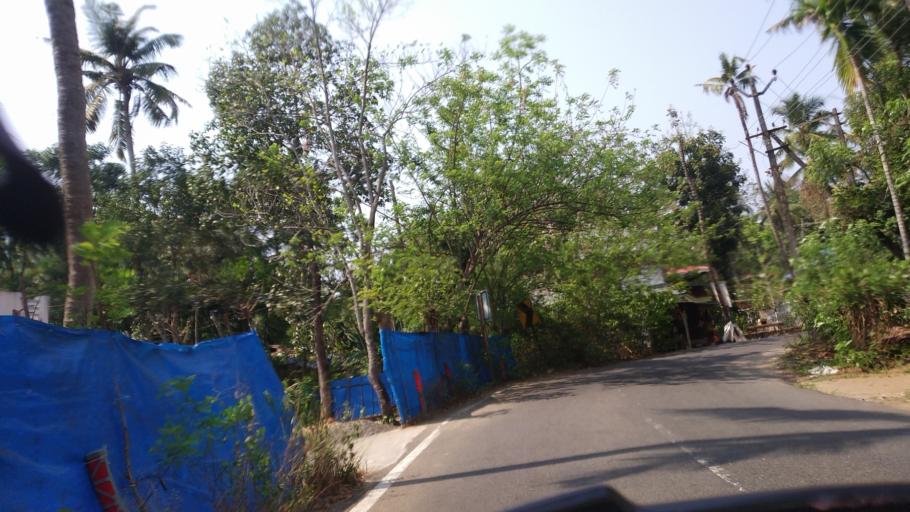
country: IN
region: Kerala
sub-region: Thrissur District
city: Thanniyam
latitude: 10.3296
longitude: 76.1214
